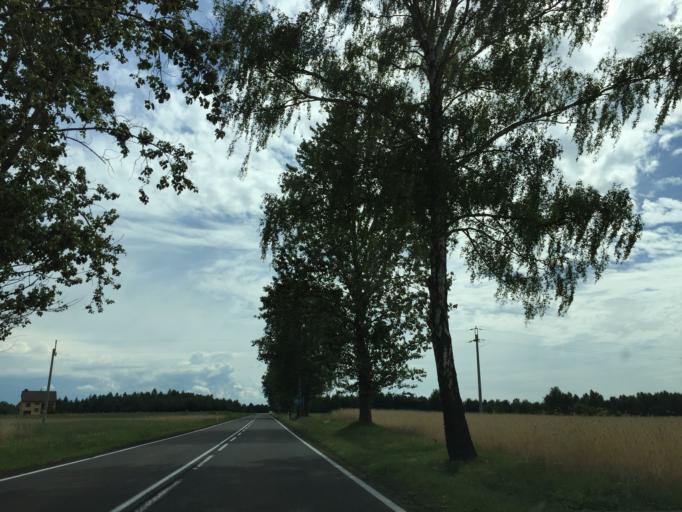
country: PL
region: Podlasie
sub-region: Powiat siemiatycki
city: Siemiatycze
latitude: 52.4780
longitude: 22.8782
